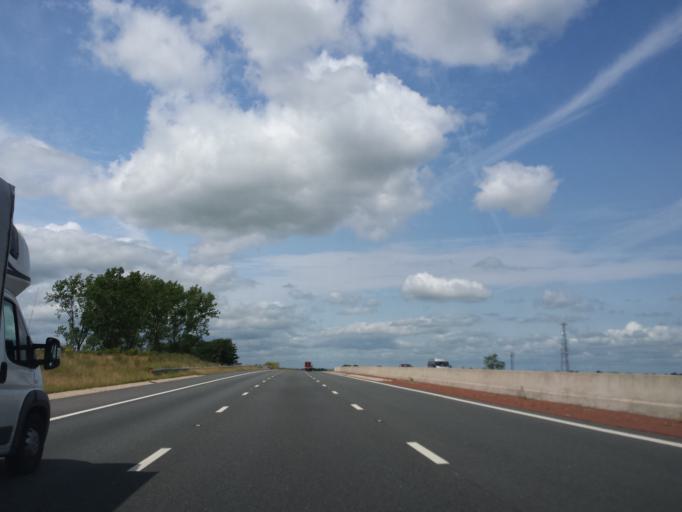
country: GB
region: England
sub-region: North Yorkshire
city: Ripon
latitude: 54.2225
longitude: -1.4862
